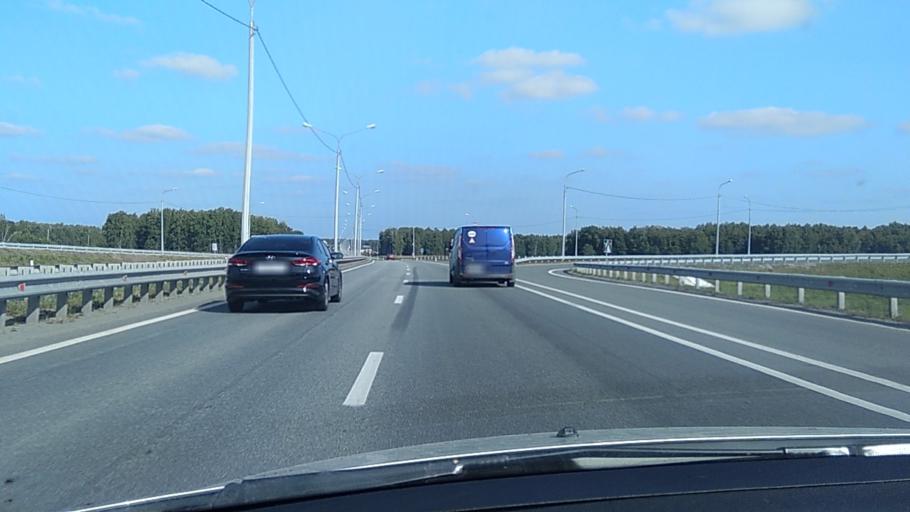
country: RU
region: Chelyabinsk
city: Timiryazevskiy
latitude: 54.9216
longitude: 60.6968
